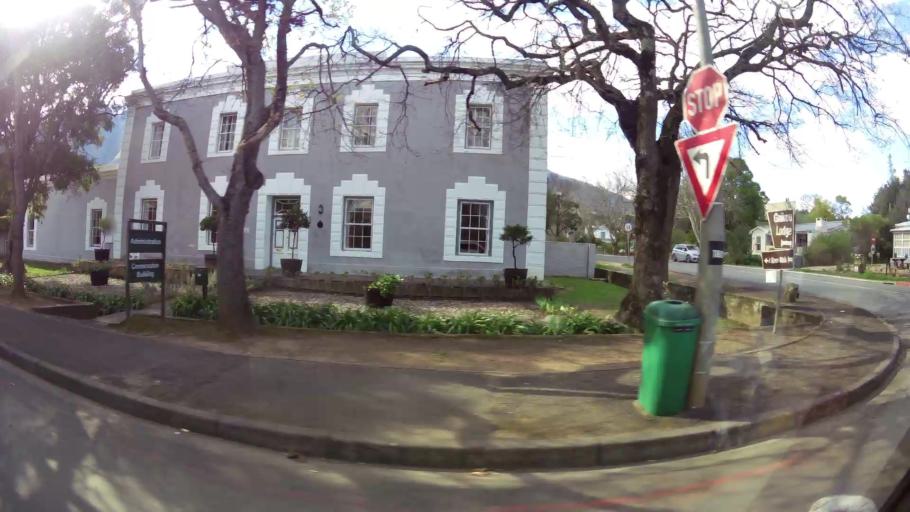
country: ZA
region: Western Cape
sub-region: Overberg District Municipality
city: Swellendam
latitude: -34.0180
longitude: 20.4517
